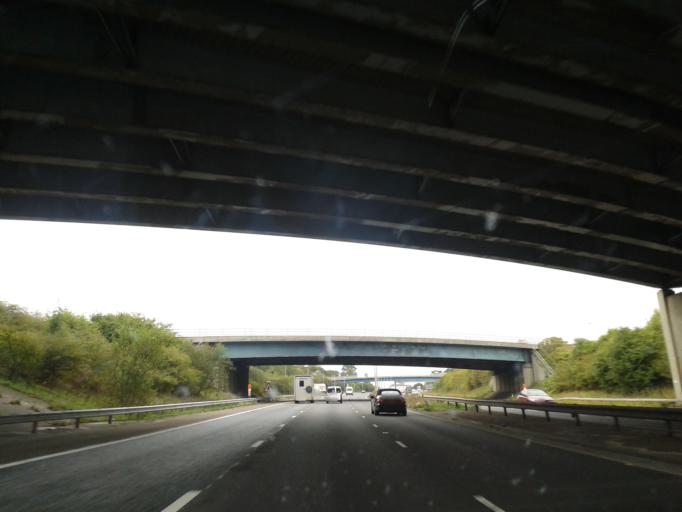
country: GB
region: England
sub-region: Lancashire
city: Clayton-le-Woods
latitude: 53.7158
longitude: -2.6610
